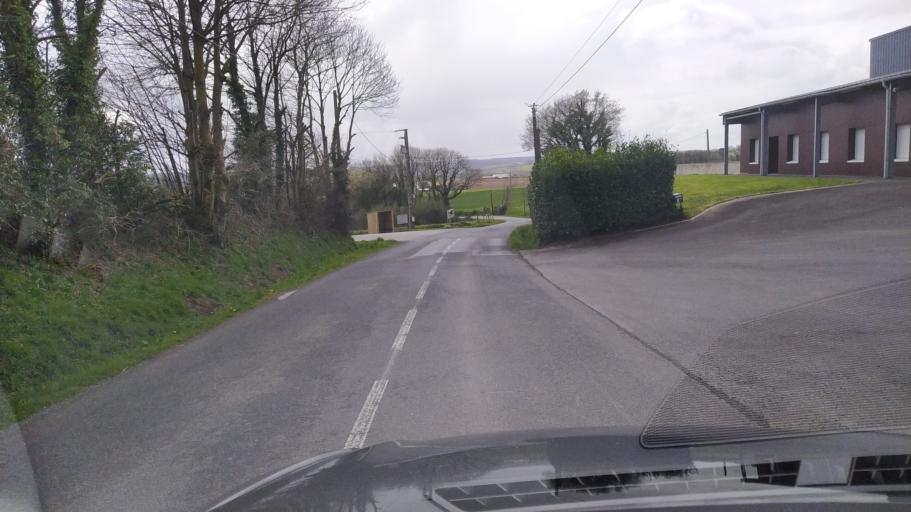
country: FR
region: Brittany
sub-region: Departement du Finistere
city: Bodilis
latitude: 48.5208
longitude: -4.1060
